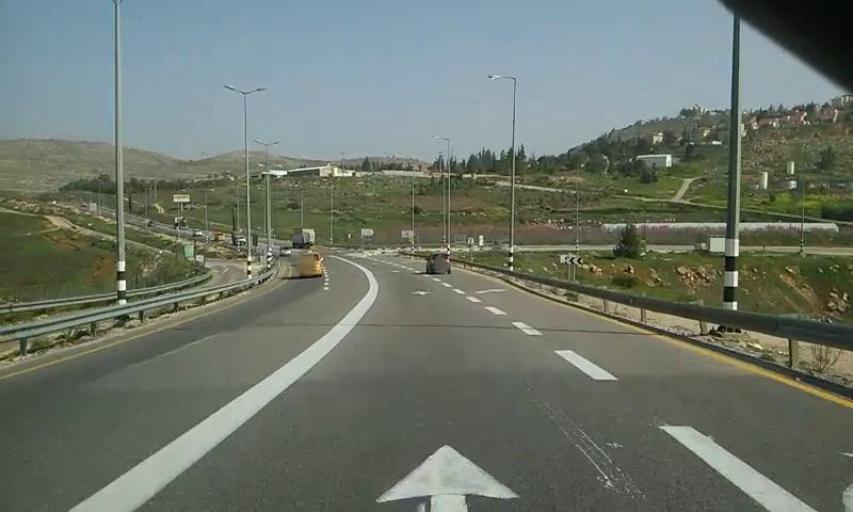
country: PS
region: West Bank
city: Turmus`ayya
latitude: 32.0526
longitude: 35.2883
